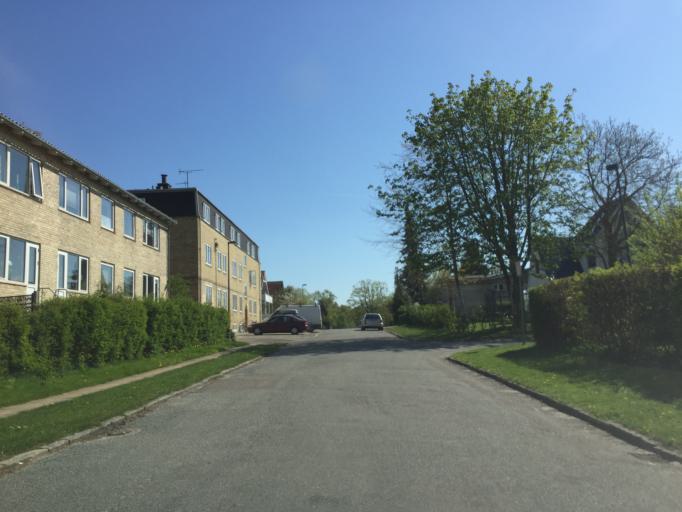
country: DK
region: Capital Region
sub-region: Frederiksberg Kommune
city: Frederiksberg
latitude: 55.7221
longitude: 12.5253
